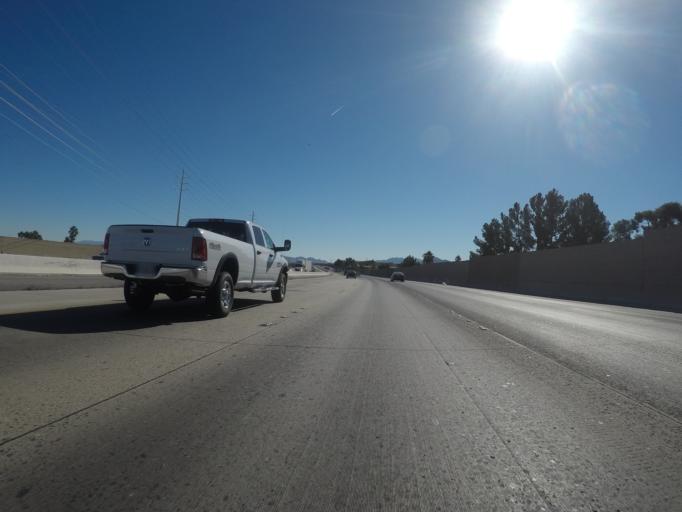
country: US
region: Nevada
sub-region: Clark County
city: Whitney
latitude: 36.0962
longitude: -115.0791
